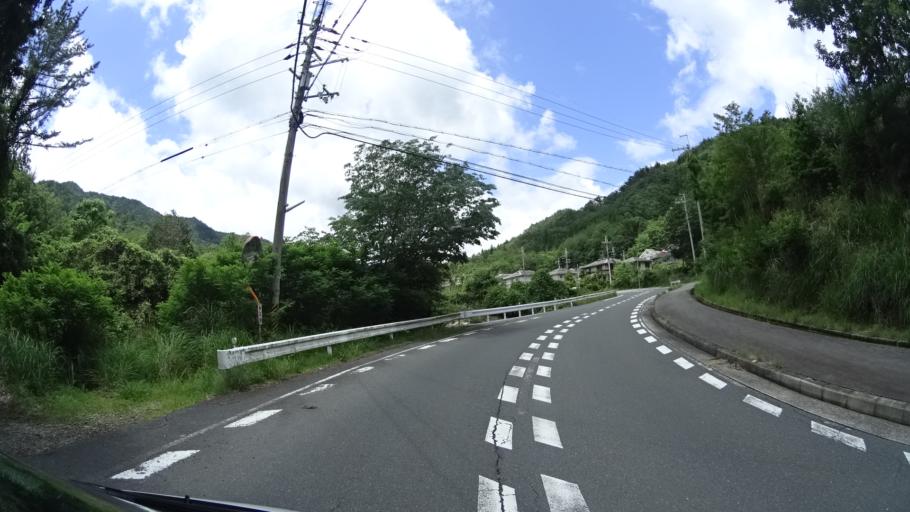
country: JP
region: Kyoto
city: Kameoka
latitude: 35.0172
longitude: 135.4203
